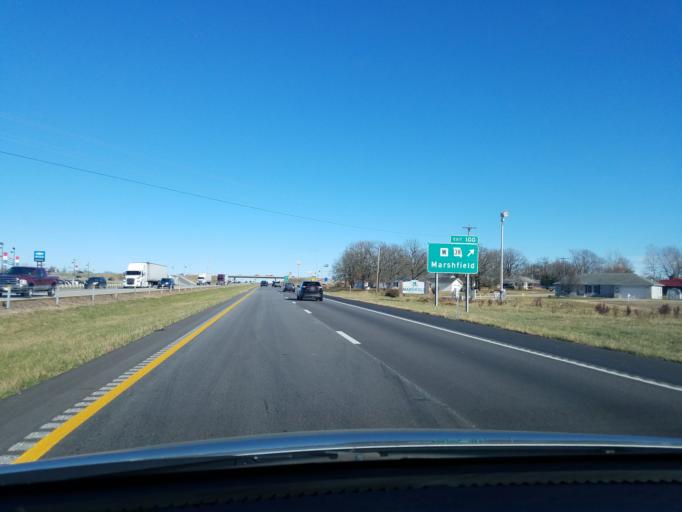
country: US
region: Missouri
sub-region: Webster County
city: Marshfield
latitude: 37.3395
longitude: -92.9341
